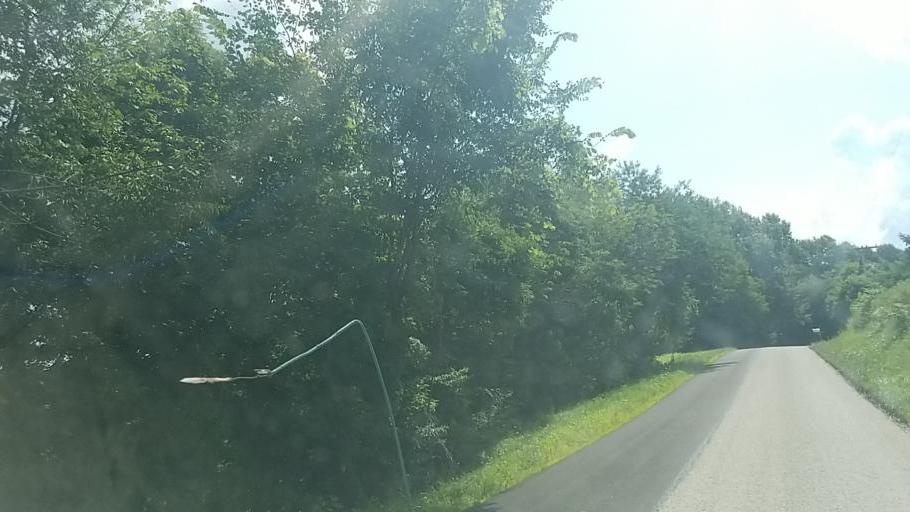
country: US
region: Ohio
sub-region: Ashland County
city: Loudonville
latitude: 40.6767
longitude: -82.3714
